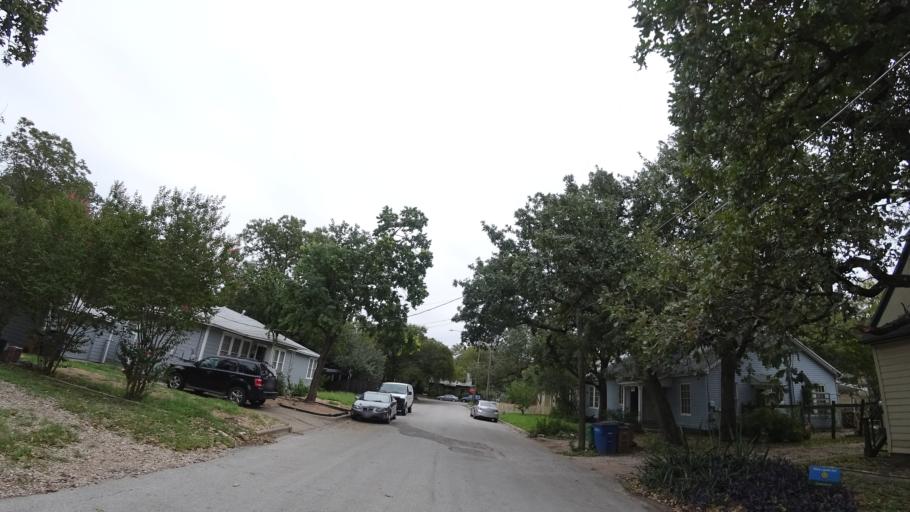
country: US
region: Texas
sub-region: Travis County
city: Austin
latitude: 30.2879
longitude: -97.7220
